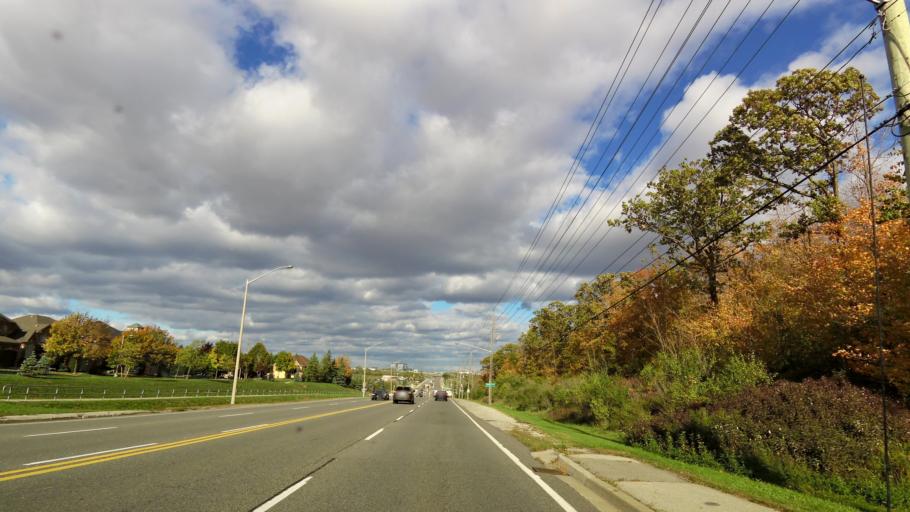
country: CA
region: Ontario
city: Oakville
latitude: 43.4903
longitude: -79.6847
